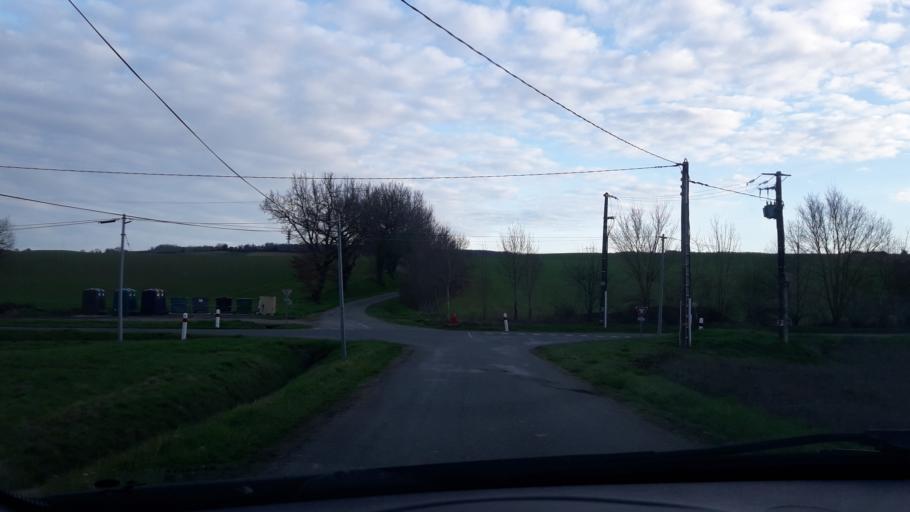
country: FR
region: Midi-Pyrenees
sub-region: Departement du Gers
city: Pujaudran
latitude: 43.6669
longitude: 1.0928
